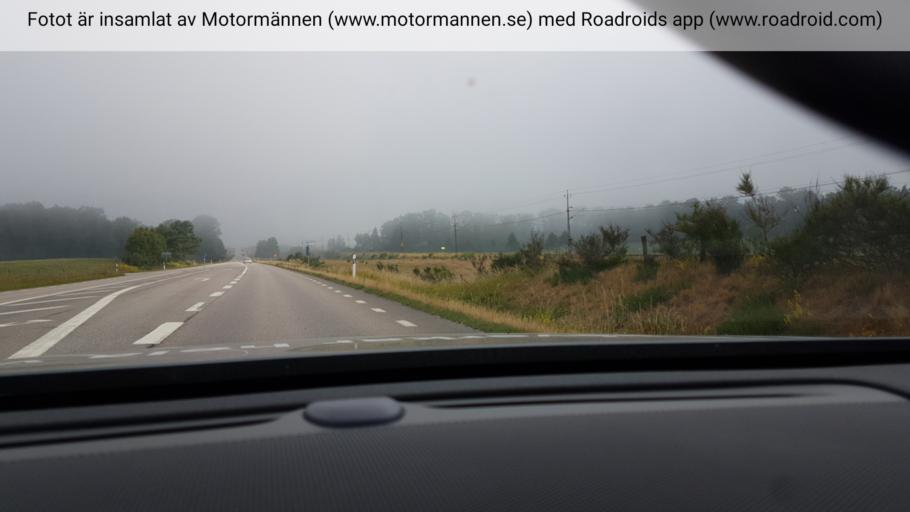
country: SE
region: Skane
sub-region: Hassleholms Kommun
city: Hassleholm
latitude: 56.1853
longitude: 13.7533
